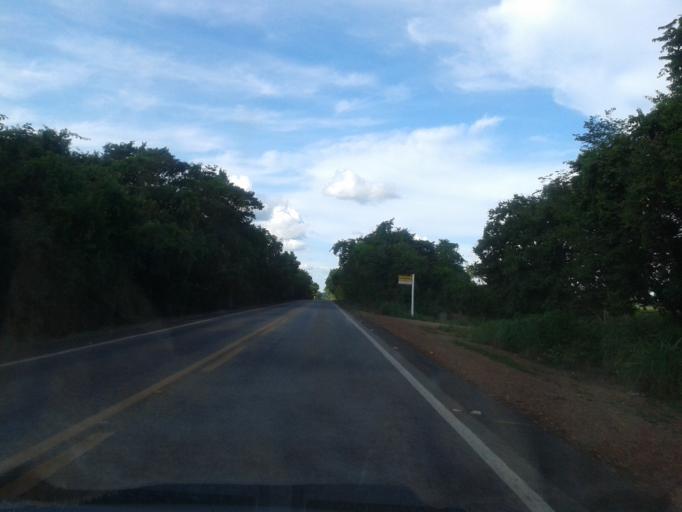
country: BR
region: Goias
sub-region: Mozarlandia
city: Mozarlandia
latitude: -14.5977
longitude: -50.5105
